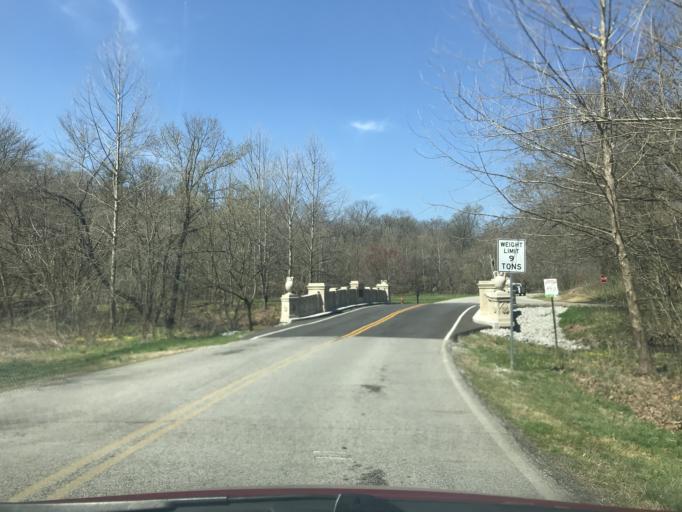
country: US
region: Kentucky
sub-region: Jefferson County
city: Saint Matthews
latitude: 38.2340
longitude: -85.6868
